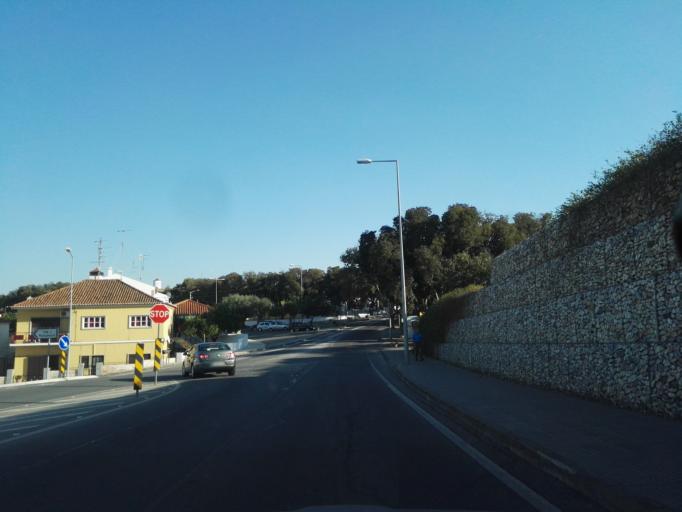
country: PT
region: Portalegre
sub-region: Elvas
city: Elvas
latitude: 38.8849
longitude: -7.1604
